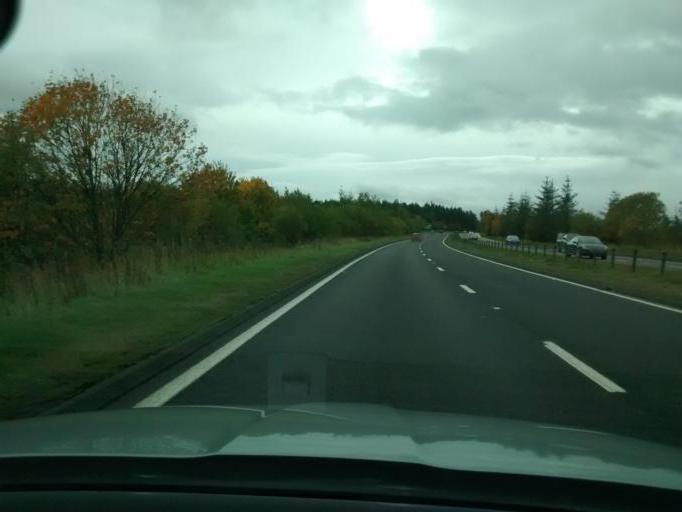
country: GB
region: Scotland
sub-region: Perth and Kinross
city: Methven
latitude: 56.3616
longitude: -3.5571
